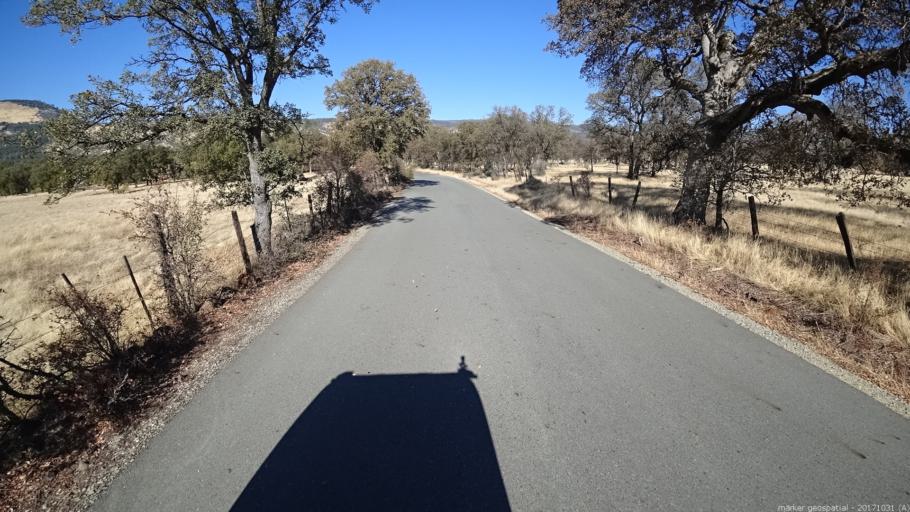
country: US
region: California
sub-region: Shasta County
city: Shingletown
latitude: 40.4292
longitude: -121.9790
